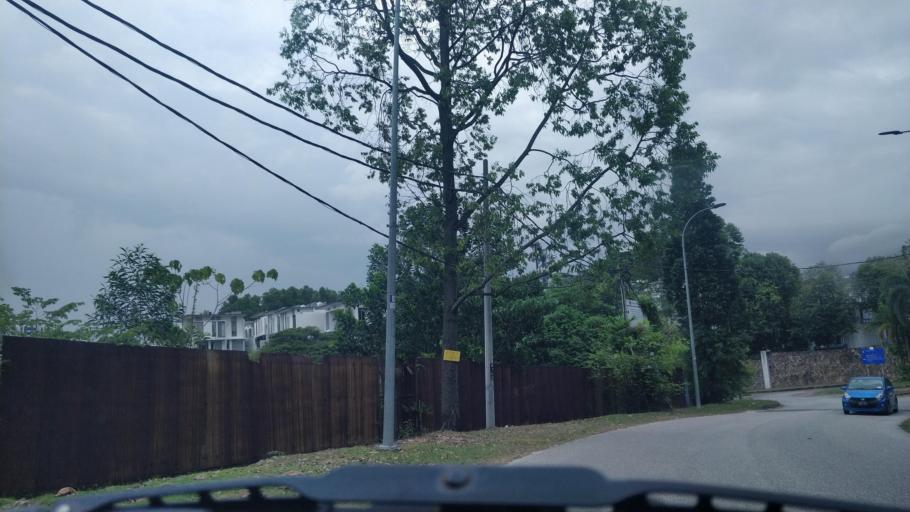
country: MY
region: Selangor
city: Kuang
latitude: 3.2068
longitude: 101.5850
